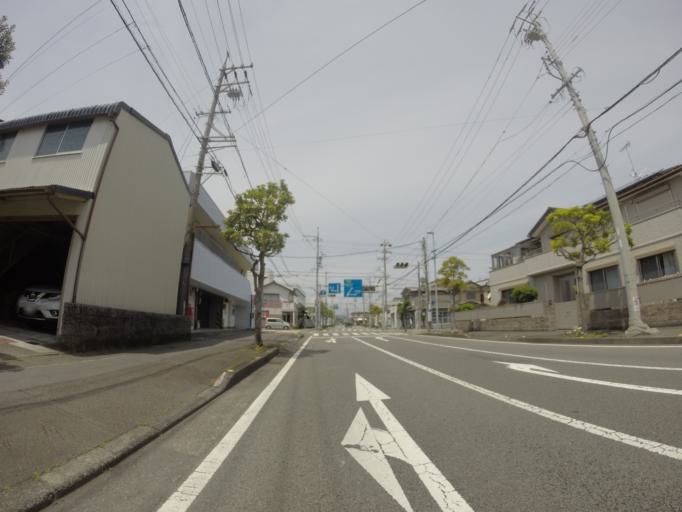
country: JP
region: Shizuoka
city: Yaizu
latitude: 34.8674
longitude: 138.3177
